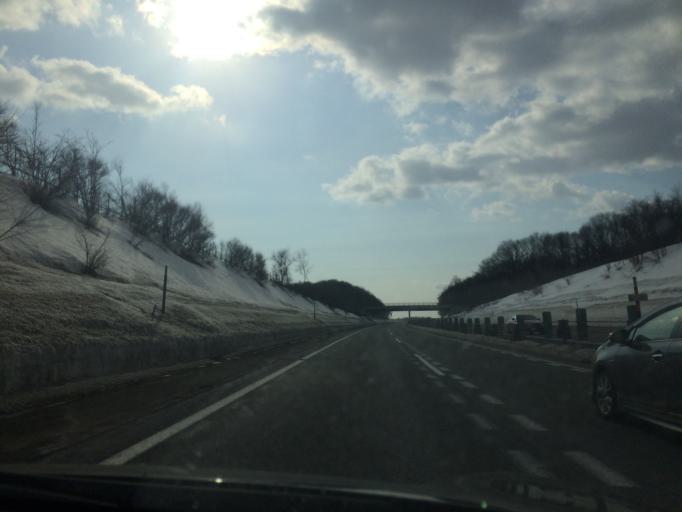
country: JP
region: Hokkaido
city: Kitahiroshima
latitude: 42.9204
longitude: 141.5445
